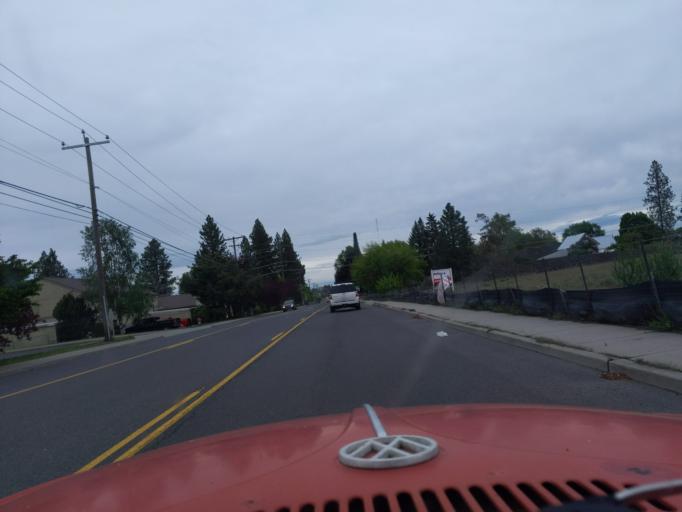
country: US
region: Washington
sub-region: Spokane County
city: Spokane
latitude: 47.6045
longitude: -117.3684
